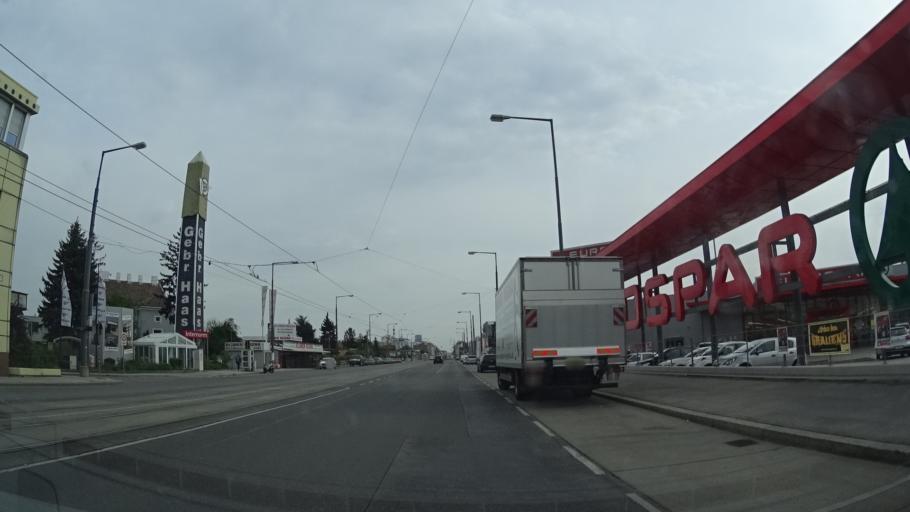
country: AT
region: Lower Austria
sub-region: Politischer Bezirk Korneuburg
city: Langenzersdorf
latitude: 48.2757
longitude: 16.3888
